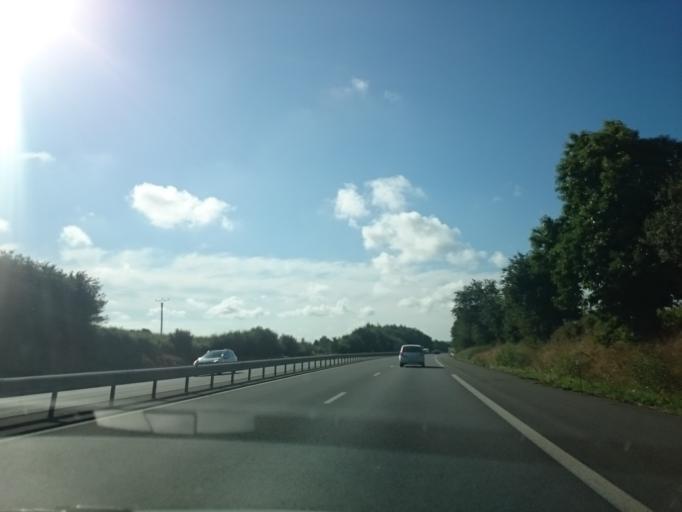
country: FR
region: Brittany
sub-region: Departement des Cotes-d'Armor
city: Broons
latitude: 48.3105
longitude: -2.2394
